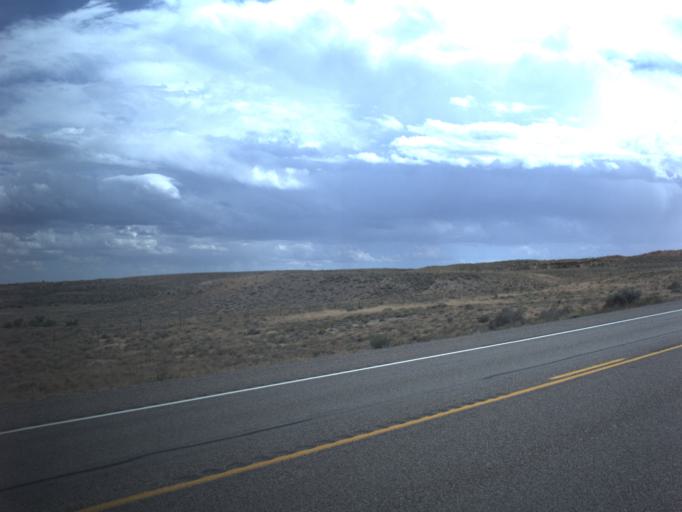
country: US
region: Utah
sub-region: Carbon County
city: Price
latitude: 39.5013
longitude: -110.8400
